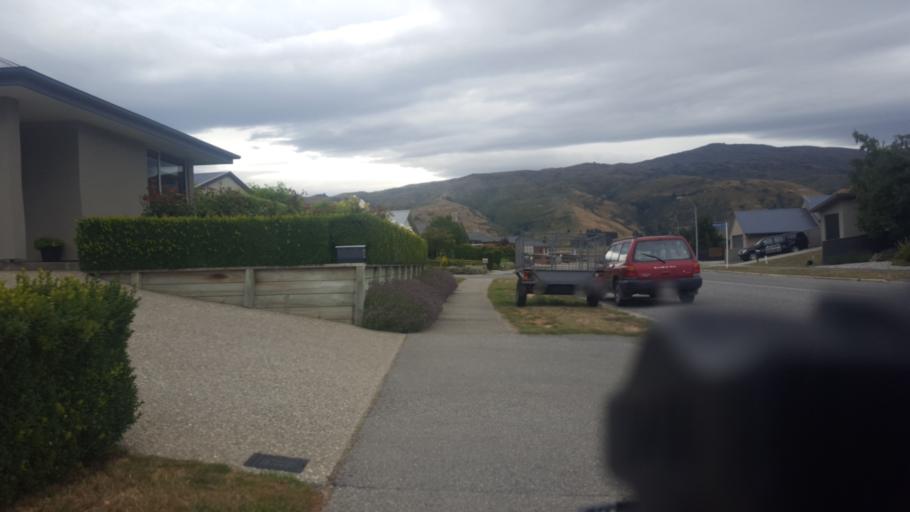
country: NZ
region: Otago
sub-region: Queenstown-Lakes District
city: Wanaka
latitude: -45.0456
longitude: 169.1818
